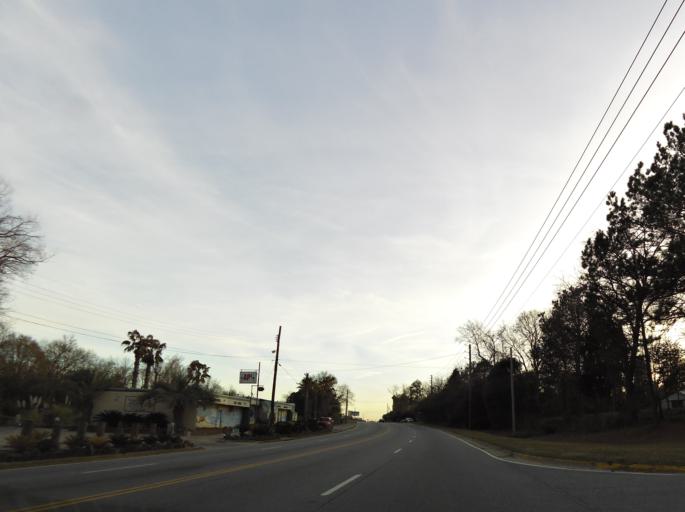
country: US
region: Georgia
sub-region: Bibb County
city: Macon
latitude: 32.7880
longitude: -83.6523
